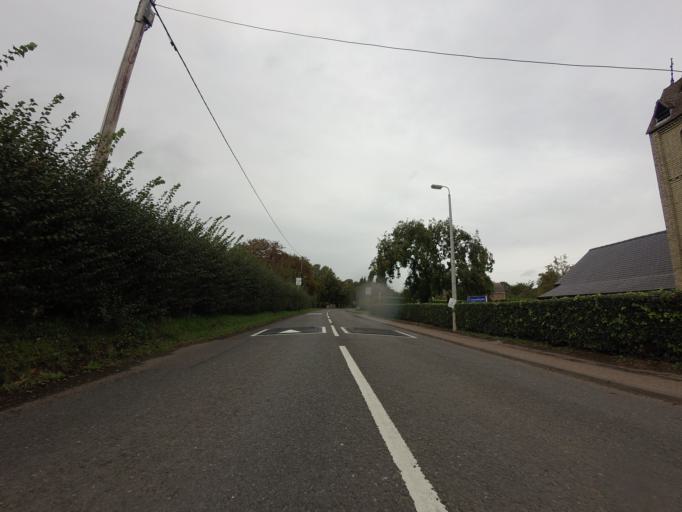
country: GB
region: England
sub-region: Cambridgeshire
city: Harston
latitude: 52.0901
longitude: 0.0732
